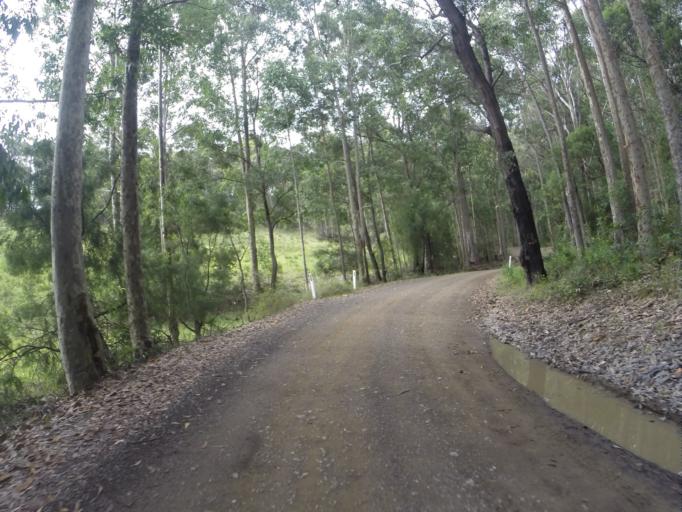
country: AU
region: New South Wales
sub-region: Eurobodalla
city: Broulee
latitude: -35.8097
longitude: 150.2131
